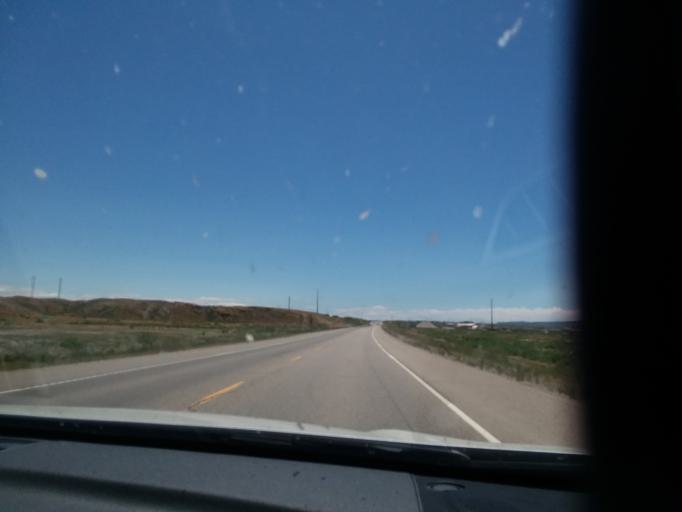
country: US
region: Wyoming
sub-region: Sweetwater County
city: North Rock Springs
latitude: 41.6385
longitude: -109.2294
